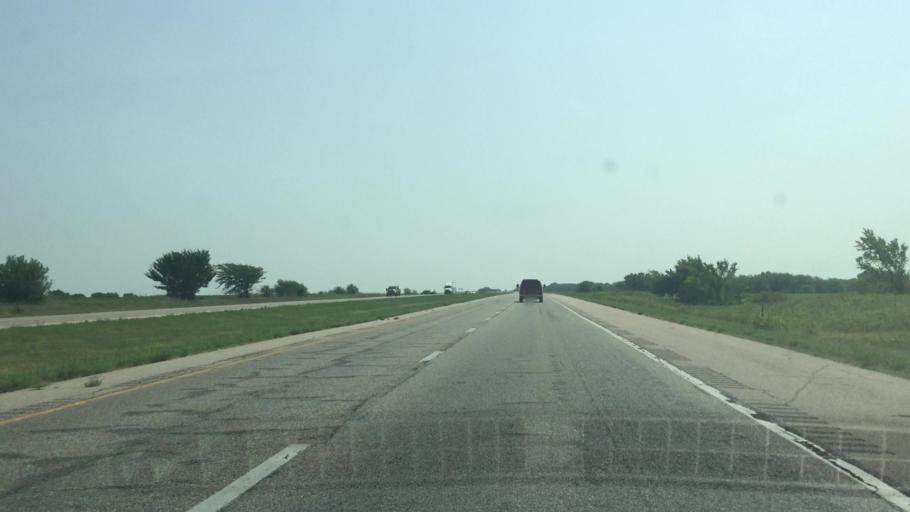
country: US
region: Kansas
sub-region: Osage County
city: Lyndon
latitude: 38.4265
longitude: -95.7649
